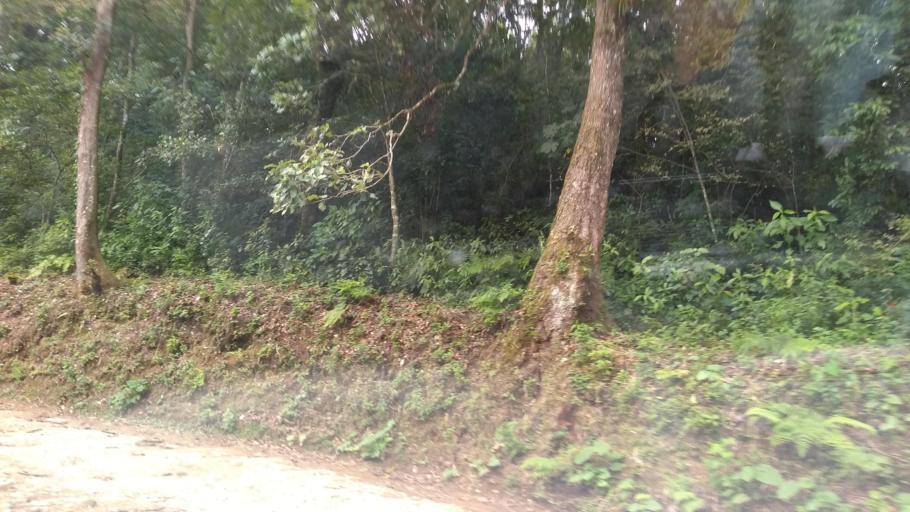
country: MX
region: Veracruz
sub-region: Tlalnelhuayocan
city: Guadalupe Victoria
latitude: 19.5399
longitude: -96.9694
